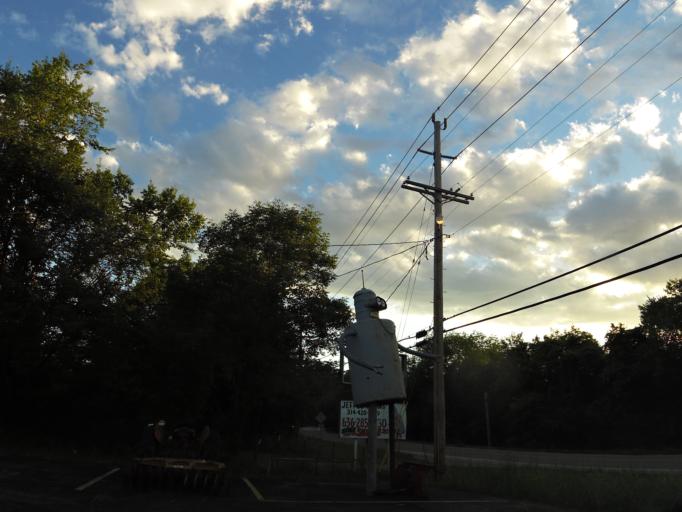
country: US
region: Missouri
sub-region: Jefferson County
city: Cedar Hill
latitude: 38.3314
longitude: -90.6924
